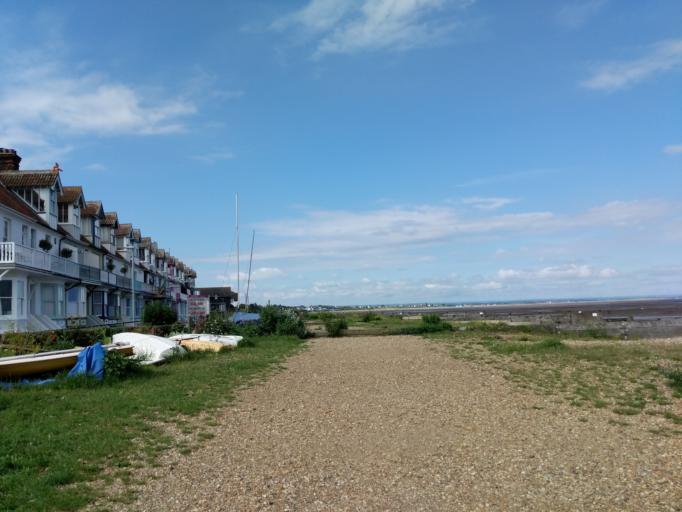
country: GB
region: England
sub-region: Kent
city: Whitstable
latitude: 51.3577
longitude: 1.0189
